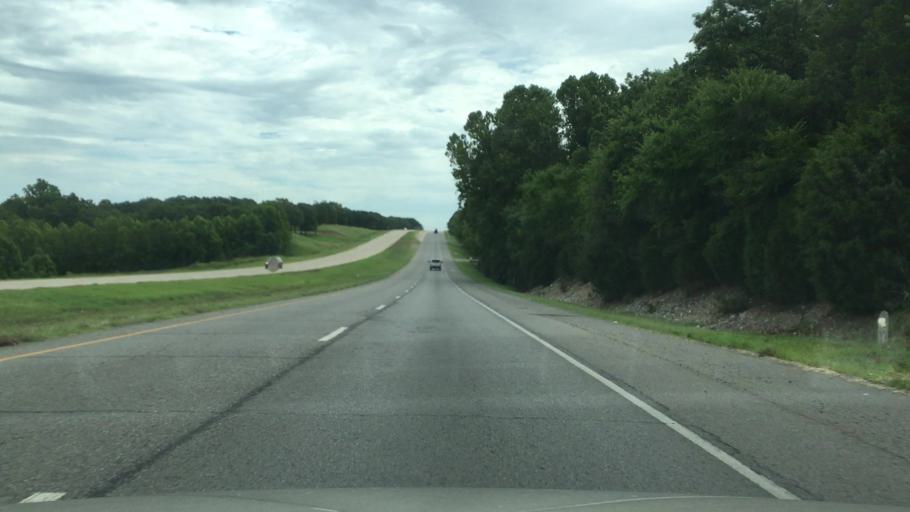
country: US
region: Oklahoma
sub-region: Cherokee County
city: Park Hill
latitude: 35.8098
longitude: -95.0699
